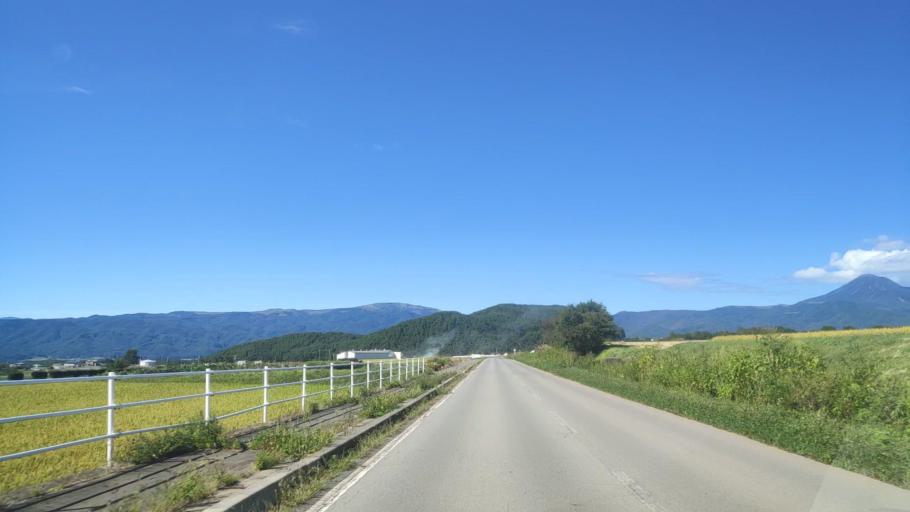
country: JP
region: Nagano
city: Chino
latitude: 35.9853
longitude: 138.2181
